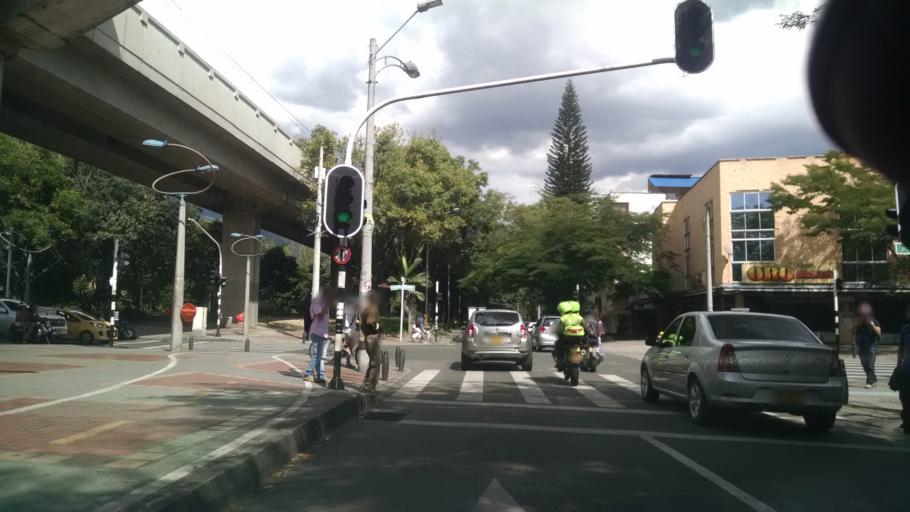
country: CO
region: Antioquia
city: Medellin
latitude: 6.2531
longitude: -75.5881
